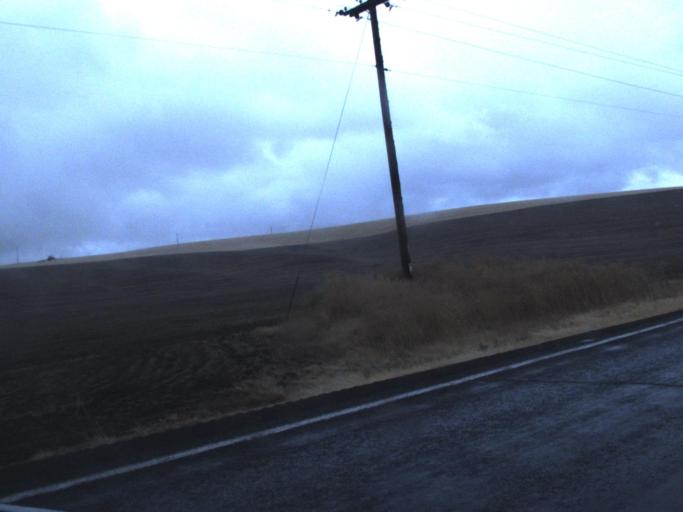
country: US
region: Washington
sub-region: Whitman County
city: Colfax
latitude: 47.0988
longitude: -117.6044
